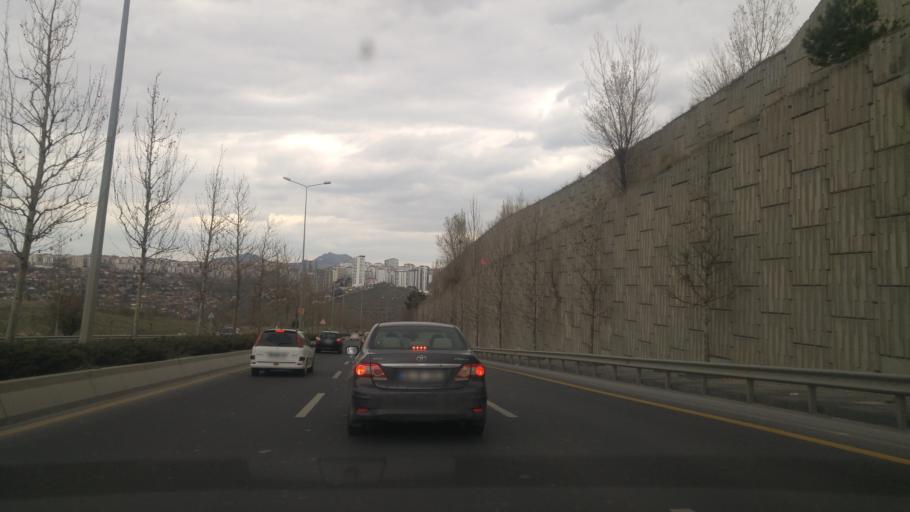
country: TR
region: Ankara
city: Cankaya
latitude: 39.8882
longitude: 32.8965
